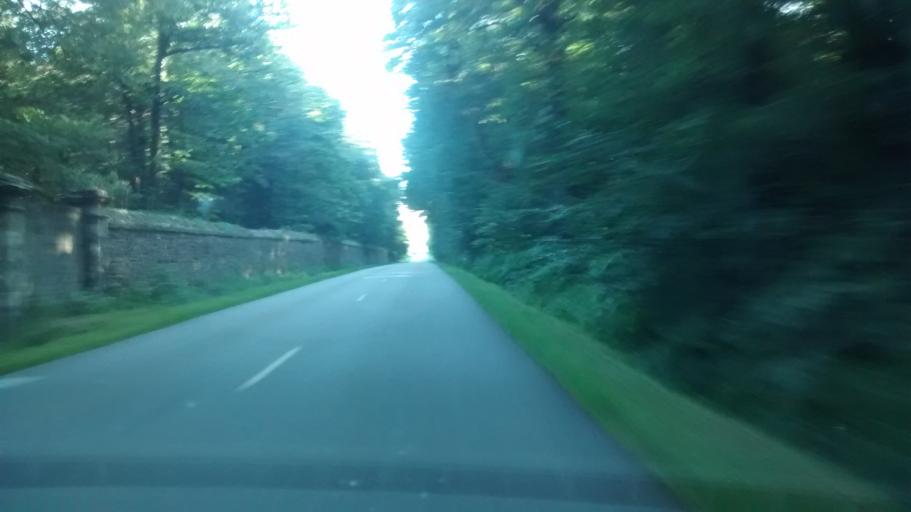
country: FR
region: Brittany
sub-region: Departement du Morbihan
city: Molac
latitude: 47.7599
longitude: -2.4367
